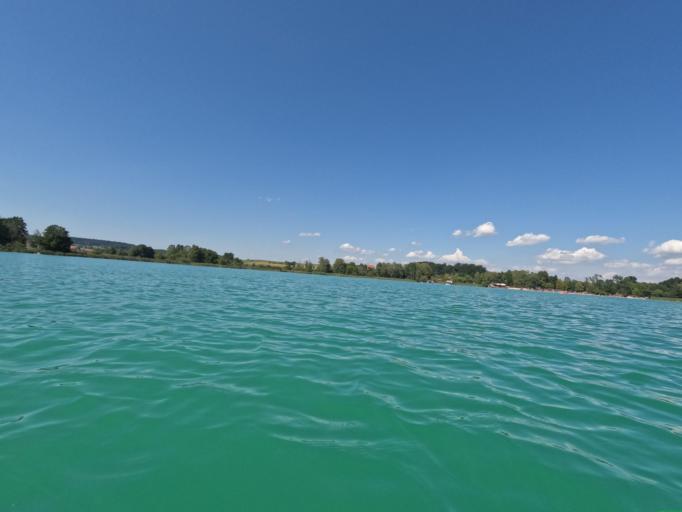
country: DE
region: Bavaria
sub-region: Upper Bavaria
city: Taching am See
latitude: 47.9844
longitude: 12.7443
